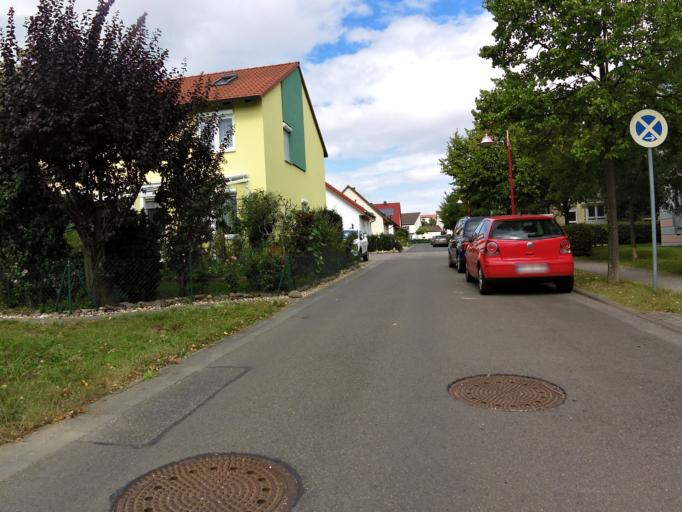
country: DE
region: Saxony
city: Leipzig
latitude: 51.3867
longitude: 12.3686
